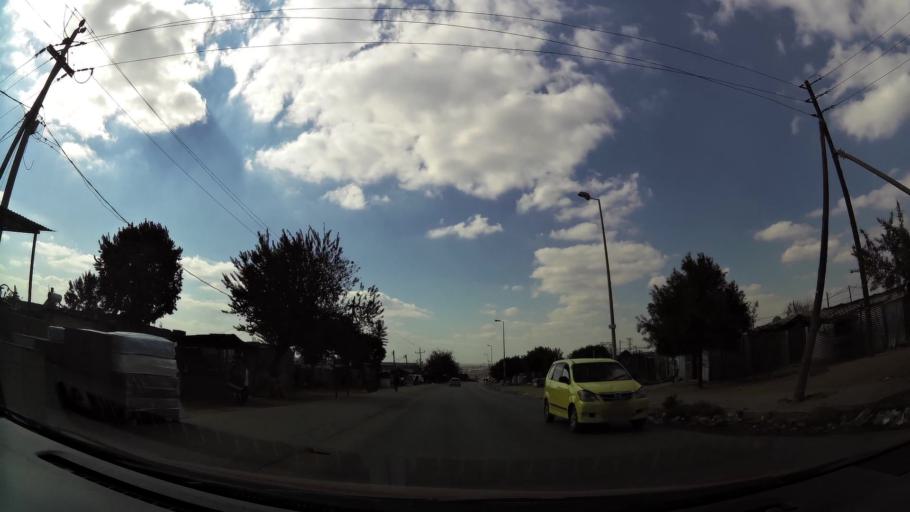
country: ZA
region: Gauteng
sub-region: Ekurhuleni Metropolitan Municipality
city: Tembisa
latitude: -26.0065
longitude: 28.1832
